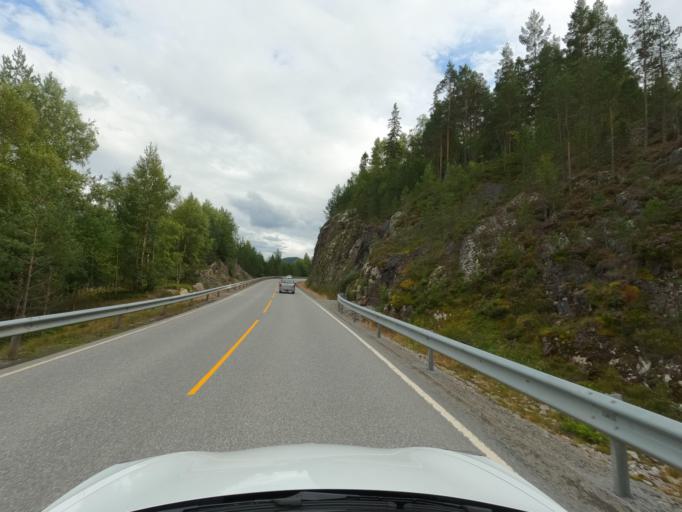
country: NO
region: Telemark
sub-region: Hjartdal
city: Sauland
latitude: 59.7843
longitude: 9.0060
